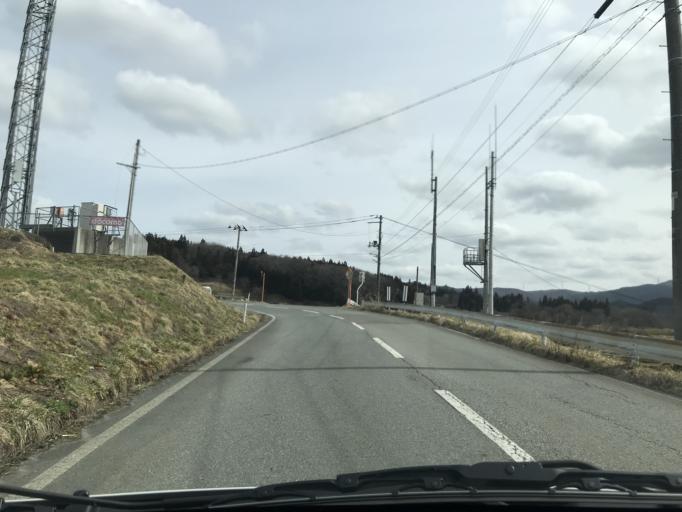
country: JP
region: Iwate
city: Kitakami
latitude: 39.2377
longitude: 141.3149
